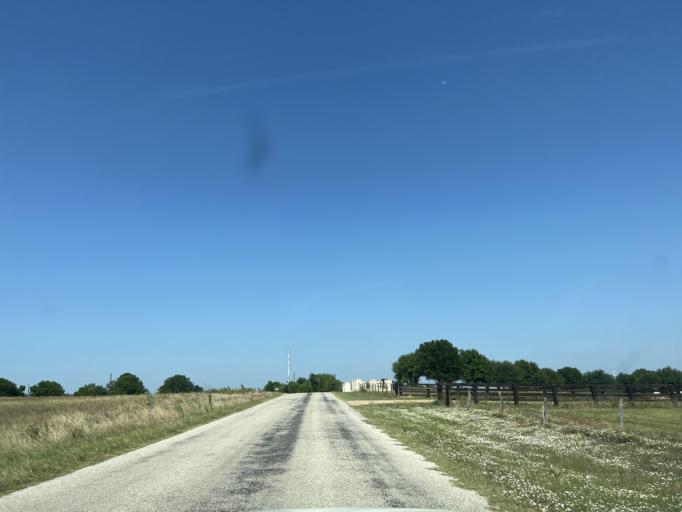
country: US
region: Texas
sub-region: Washington County
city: Brenham
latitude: 30.1731
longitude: -96.3584
